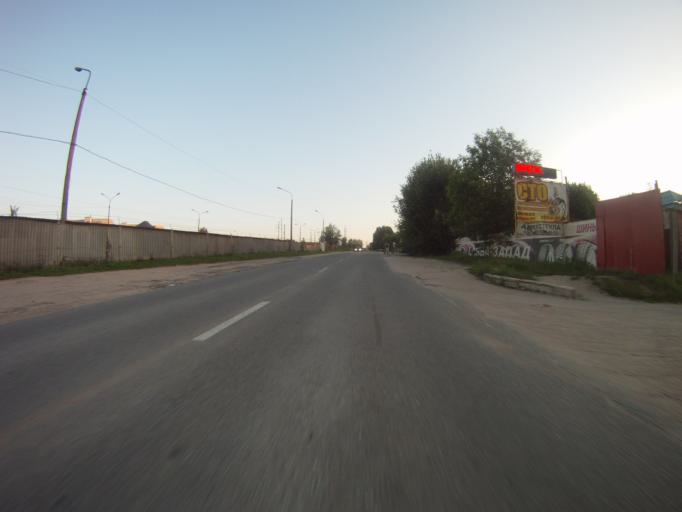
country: BY
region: Minsk
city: Novoye Medvezhino
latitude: 53.9224
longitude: 27.4720
